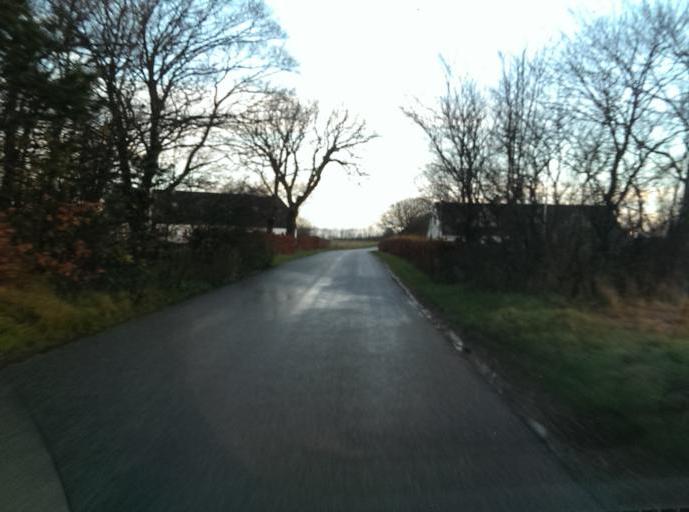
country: DK
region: South Denmark
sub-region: Esbjerg Kommune
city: Tjaereborg
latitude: 55.4805
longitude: 8.6338
